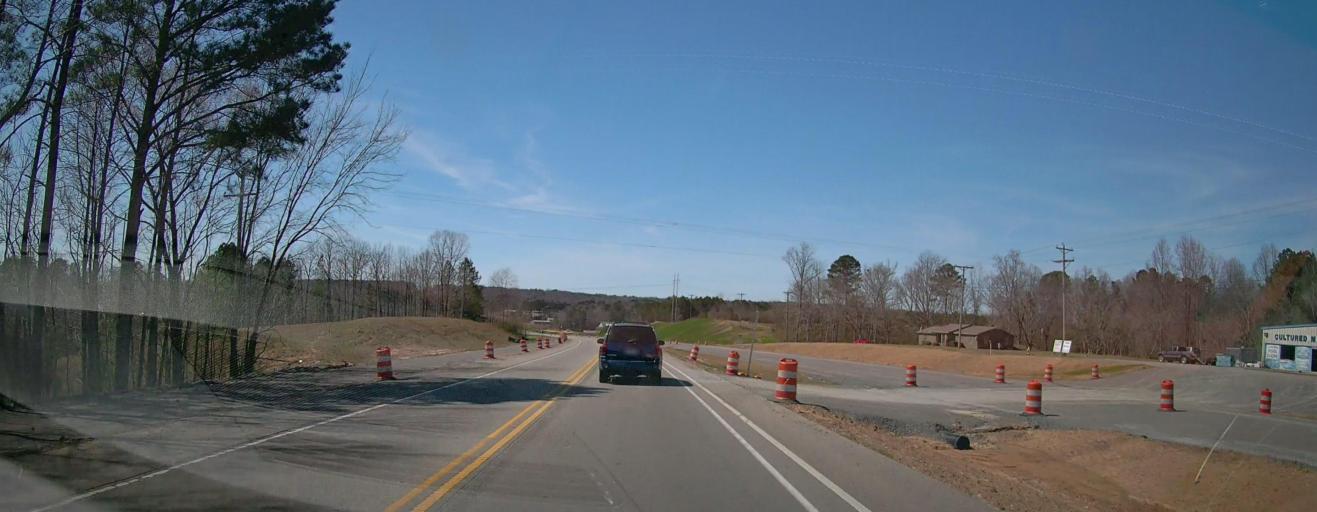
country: US
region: Alabama
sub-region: Cullman County
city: Cullman
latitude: 34.2047
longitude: -86.8324
